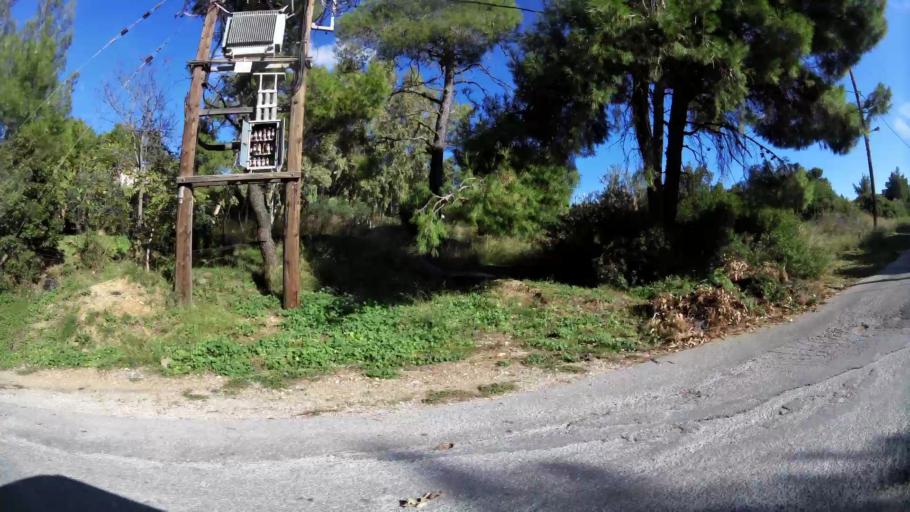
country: GR
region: Attica
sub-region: Nomarchia Athinas
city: Penteli
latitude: 38.0439
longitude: 23.8839
